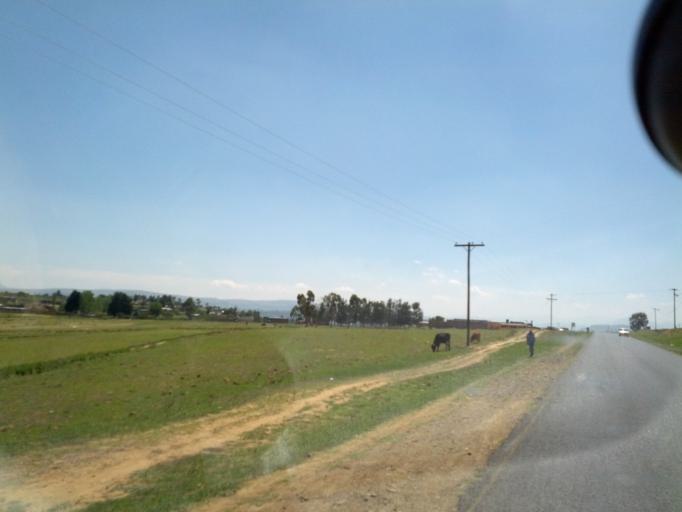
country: LS
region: Butha-Buthe
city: Butha-Buthe
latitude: -28.7797
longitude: 28.2286
